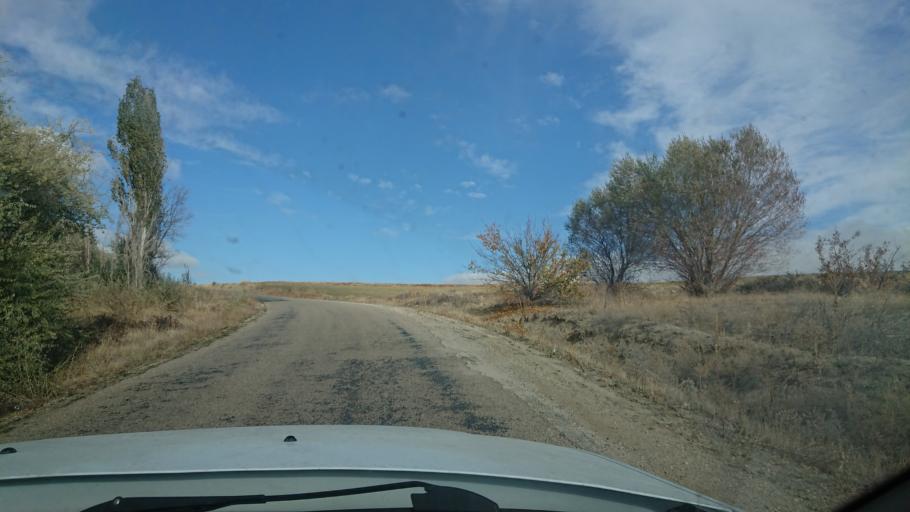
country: TR
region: Aksaray
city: Agacoren
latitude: 38.8336
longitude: 33.9557
